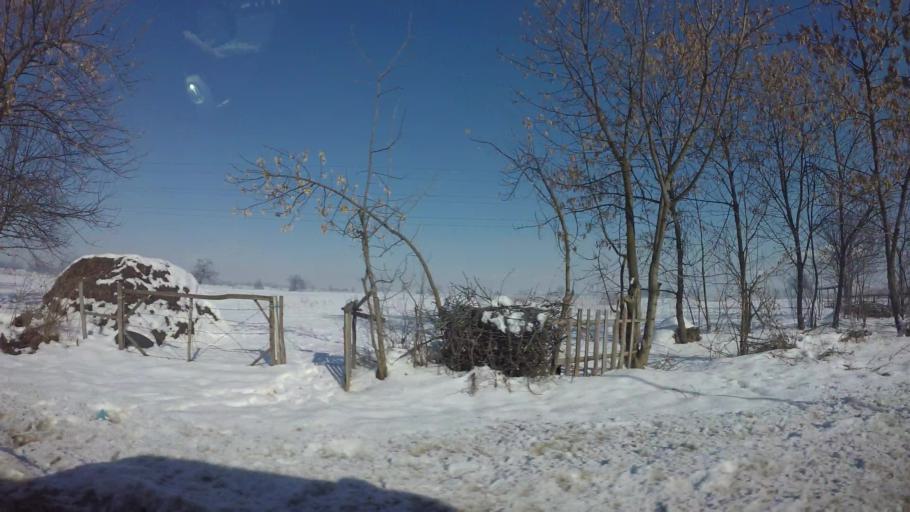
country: BA
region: Federation of Bosnia and Herzegovina
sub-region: Kanton Sarajevo
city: Sarajevo
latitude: 43.7934
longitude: 18.3281
